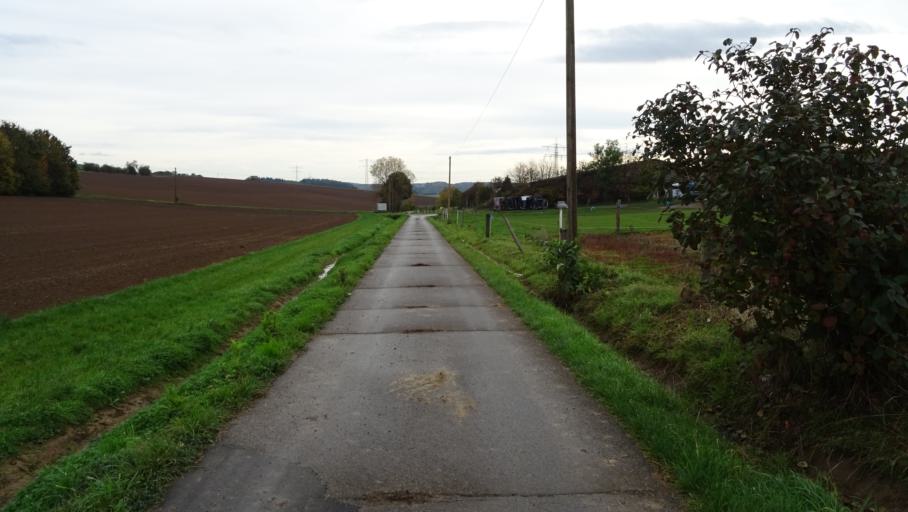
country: DE
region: Baden-Wuerttemberg
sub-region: Karlsruhe Region
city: Billigheim
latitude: 49.3456
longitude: 9.2100
